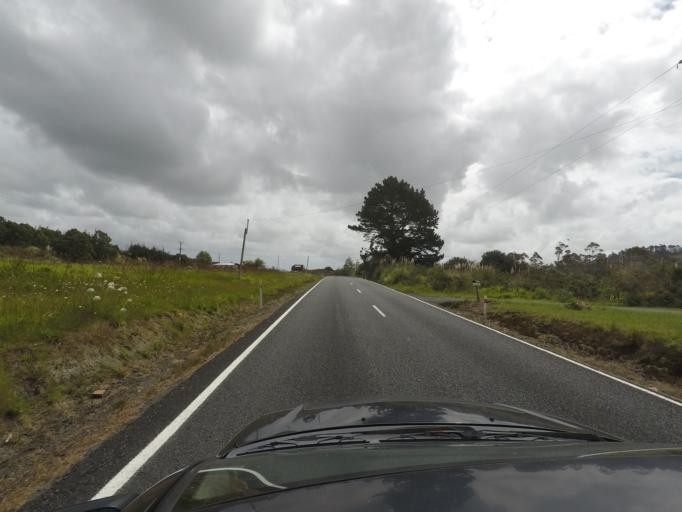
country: NZ
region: Auckland
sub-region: Auckland
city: Parakai
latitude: -36.5059
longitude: 174.4672
